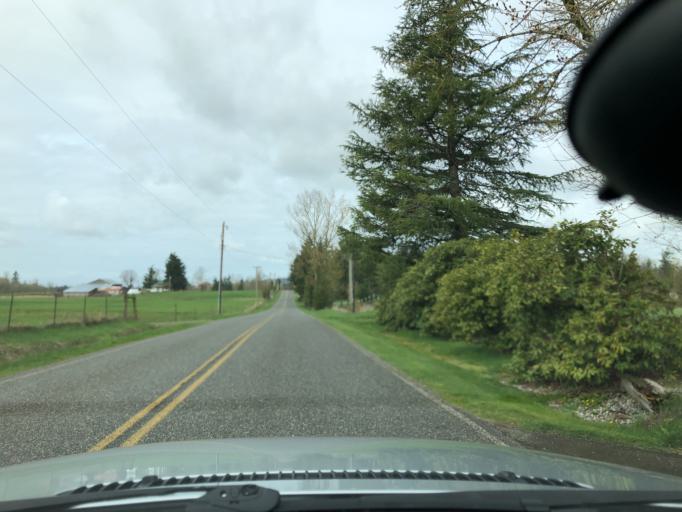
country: CA
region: British Columbia
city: Langley
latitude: 48.9794
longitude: -122.5763
